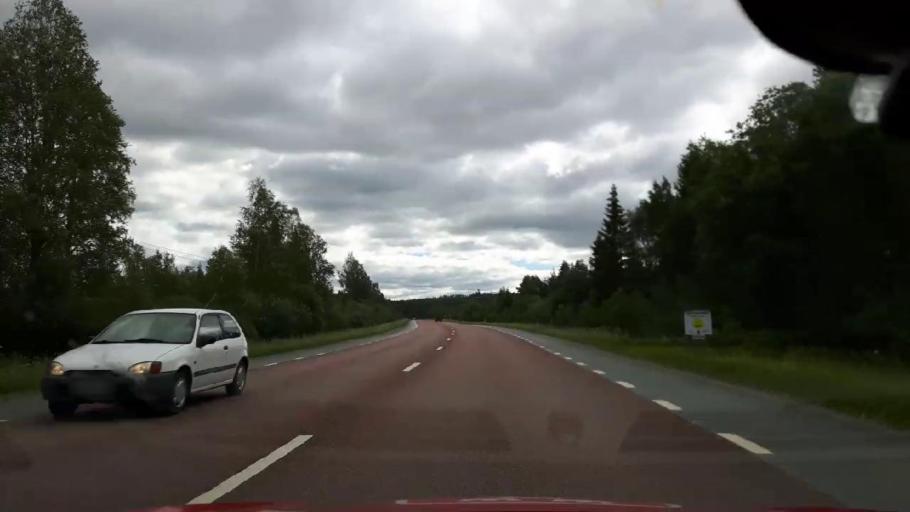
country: SE
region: Jaemtland
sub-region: Braecke Kommun
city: Braecke
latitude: 62.8181
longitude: 15.3376
